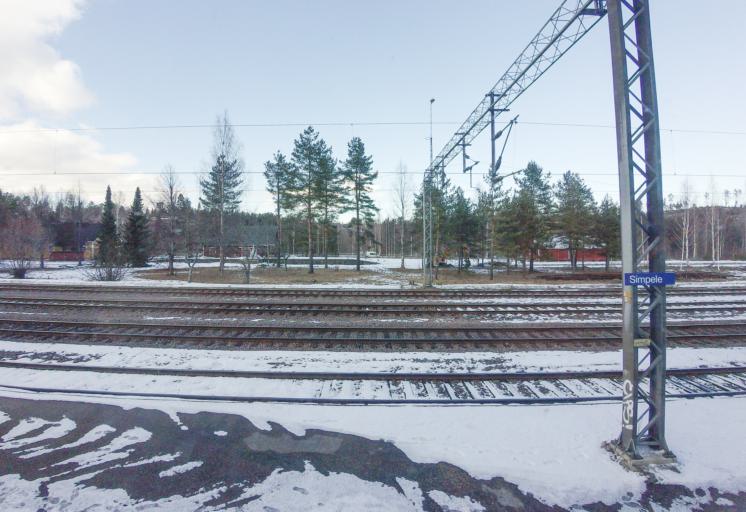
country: FI
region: South Karelia
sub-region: Imatra
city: Simpele
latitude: 61.4249
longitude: 29.3724
